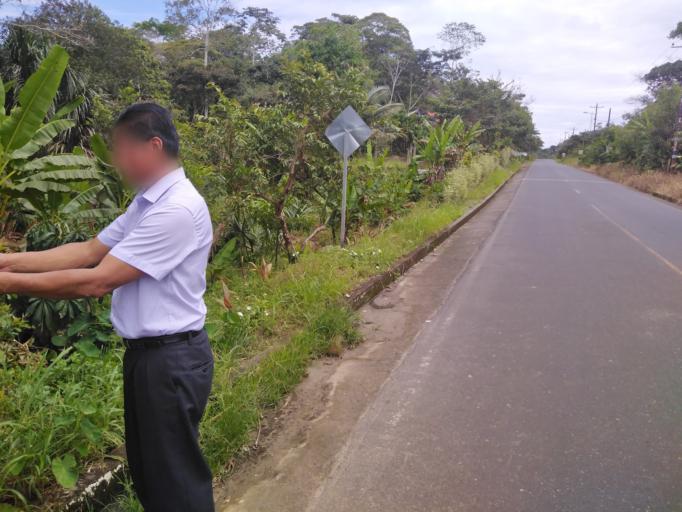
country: EC
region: Napo
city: Tena
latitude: -1.0593
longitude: -77.5493
